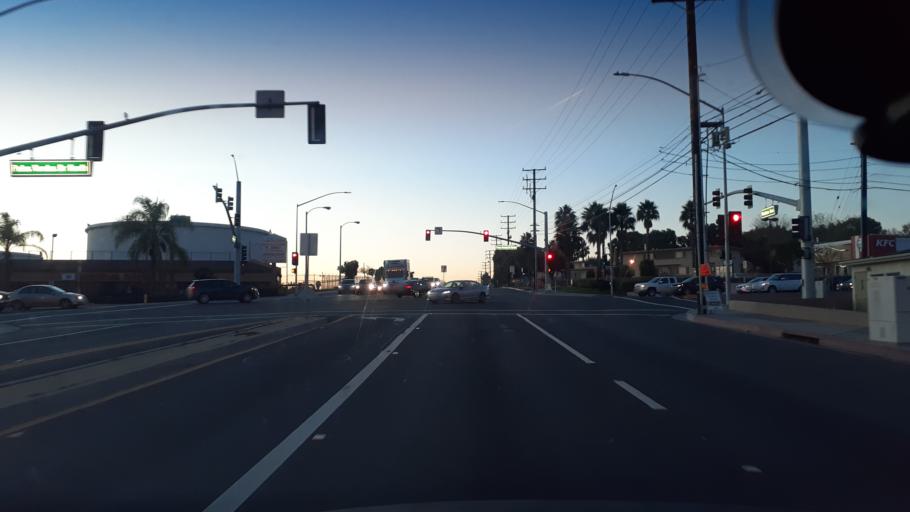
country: US
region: California
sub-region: Los Angeles County
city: Lomita
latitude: 33.7795
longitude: -118.3096
